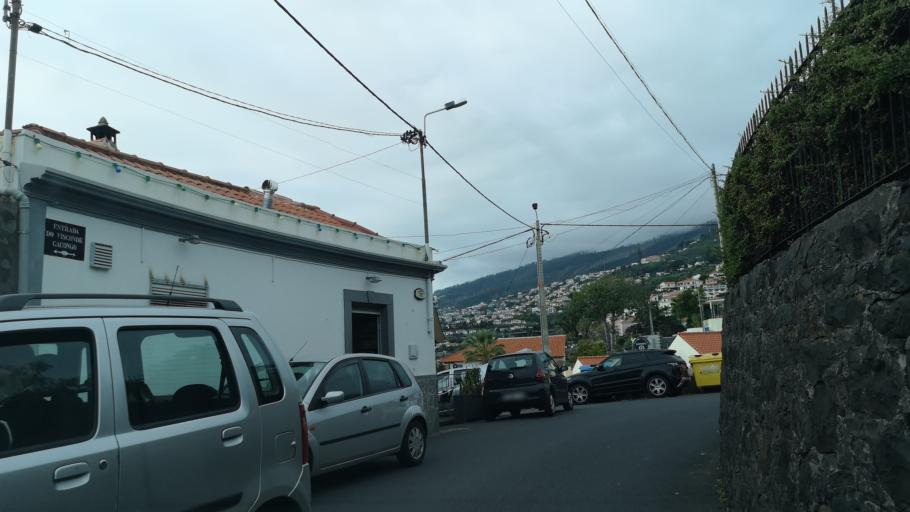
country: PT
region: Madeira
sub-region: Funchal
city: Nossa Senhora do Monte
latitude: 32.6558
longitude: -16.8944
